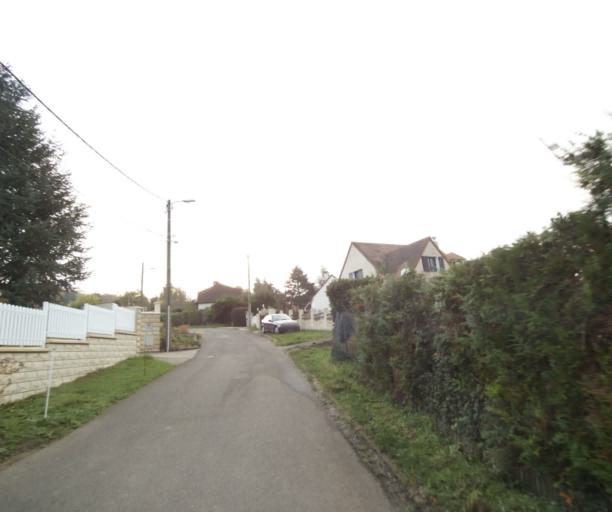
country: FR
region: Ile-de-France
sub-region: Departement des Yvelines
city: Triel-sur-Seine
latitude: 48.9923
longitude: 1.9942
